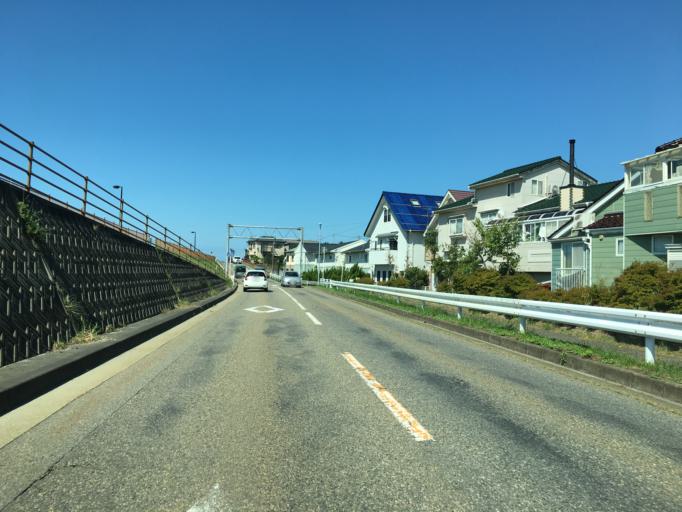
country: JP
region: Niigata
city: Niigata-shi
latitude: 37.8994
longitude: 139.0107
